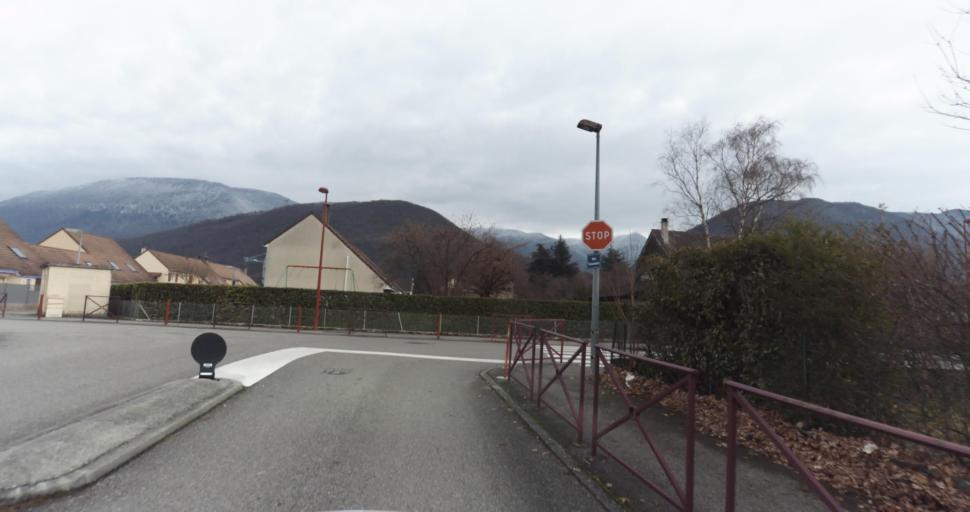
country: FR
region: Rhone-Alpes
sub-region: Departement de l'Isere
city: Vif
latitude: 45.0572
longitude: 5.6781
